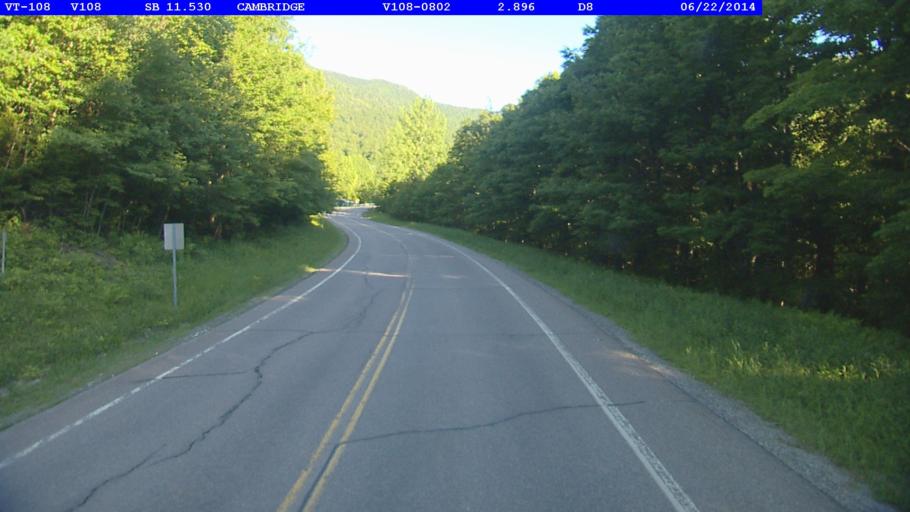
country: US
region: Vermont
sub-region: Lamoille County
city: Johnson
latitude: 44.5751
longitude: -72.7775
